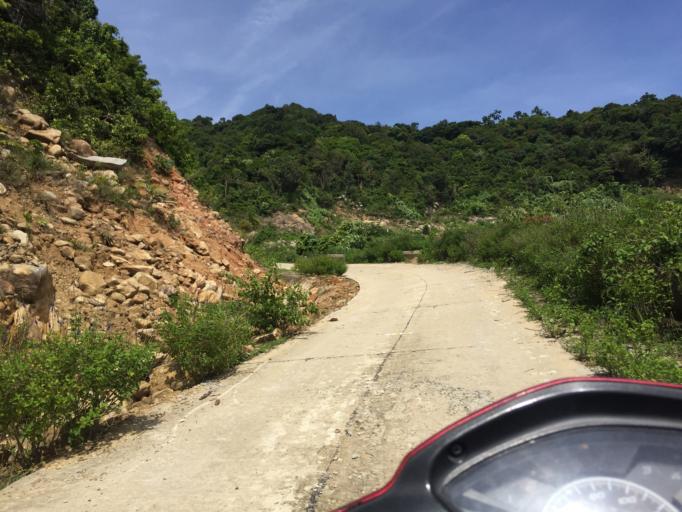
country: VN
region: Quang Nam
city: Hoi An
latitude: 15.9708
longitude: 108.5069
